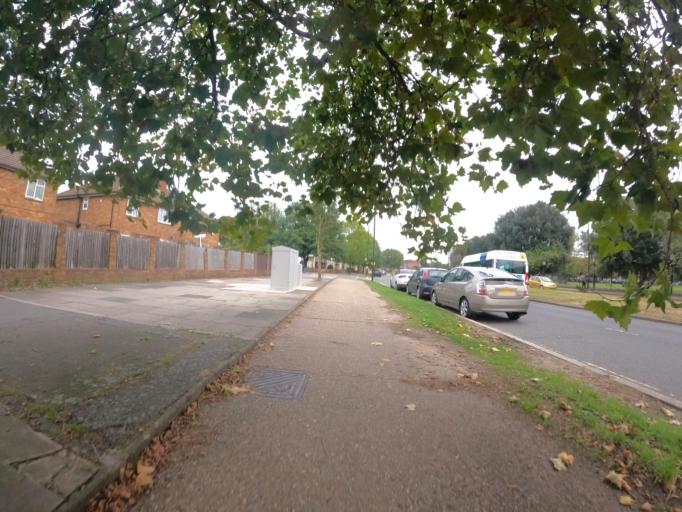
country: GB
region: England
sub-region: Greater London
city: Southall
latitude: 51.5113
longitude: -0.3688
